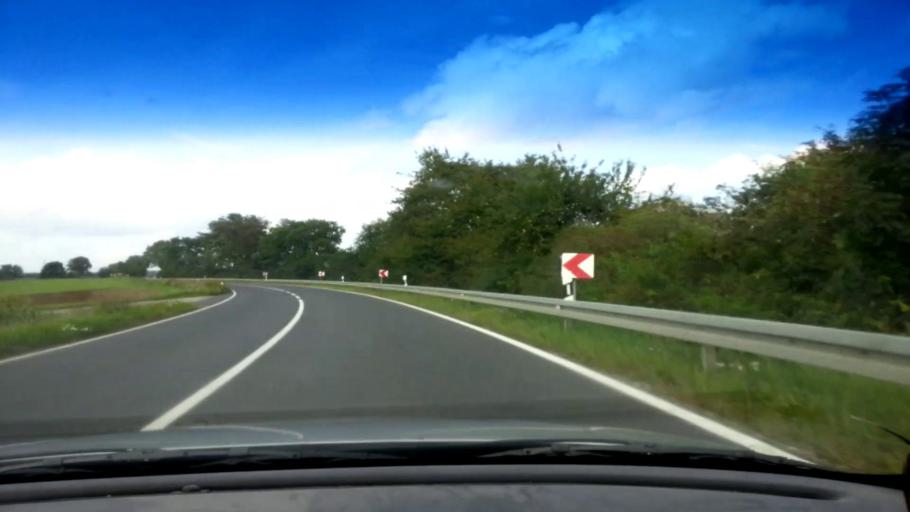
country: DE
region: Bavaria
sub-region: Upper Franconia
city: Memmelsdorf
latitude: 49.9532
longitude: 10.9940
